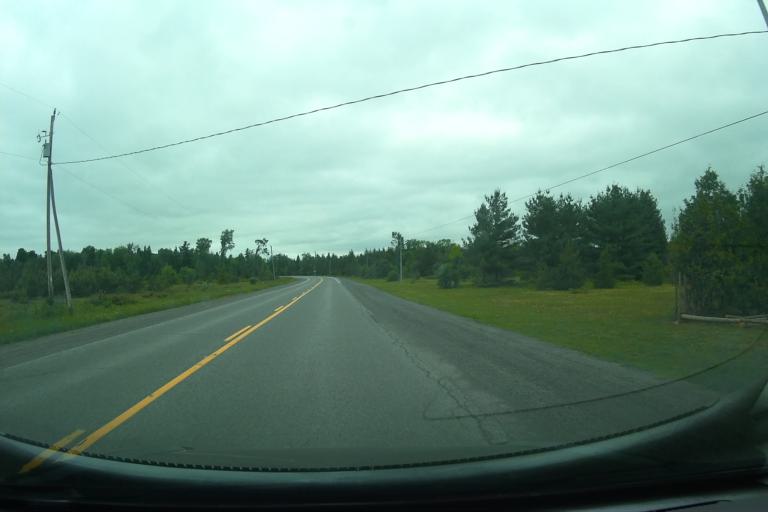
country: CA
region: Ontario
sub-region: Lanark County
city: Smiths Falls
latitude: 45.0341
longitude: -75.8608
